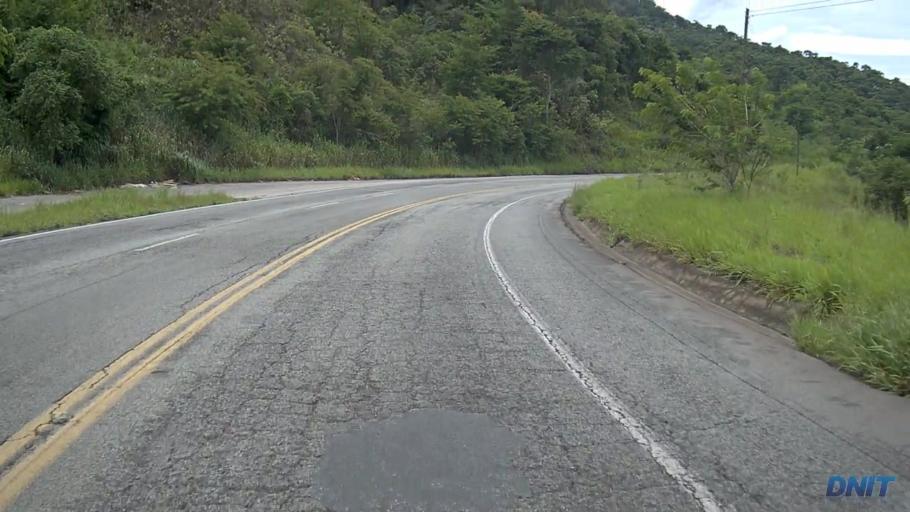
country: BR
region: Minas Gerais
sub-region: Nova Era
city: Nova Era
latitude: -19.6326
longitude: -42.8882
